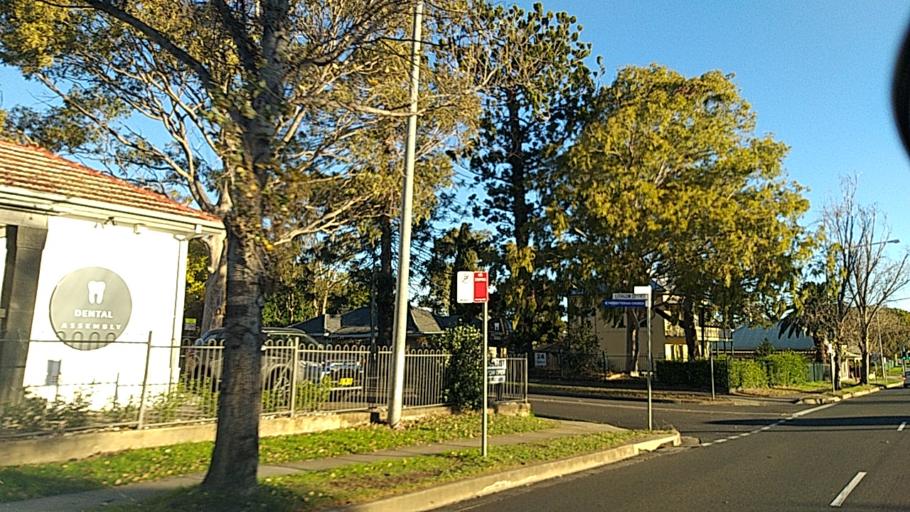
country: AU
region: New South Wales
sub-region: Campbelltown Municipality
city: Campbelltown
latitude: -34.0686
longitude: 150.8154
